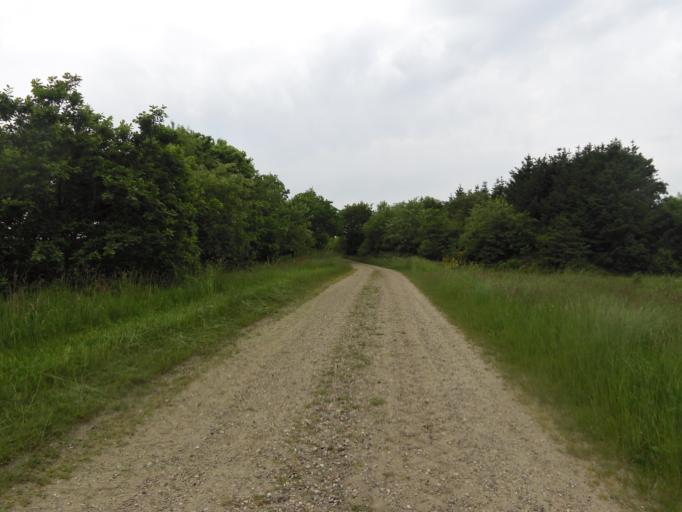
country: DK
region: South Denmark
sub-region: Esbjerg Kommune
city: Ribe
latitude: 55.3203
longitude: 8.8428
